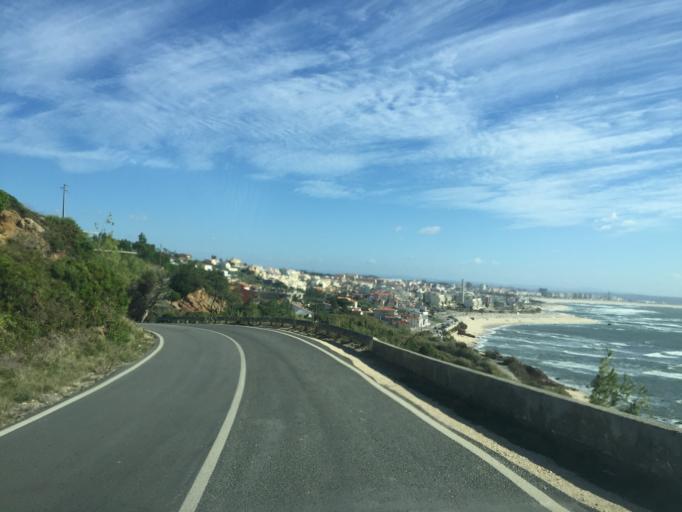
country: PT
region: Coimbra
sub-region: Figueira da Foz
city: Buarcos
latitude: 40.1791
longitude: -8.9041
